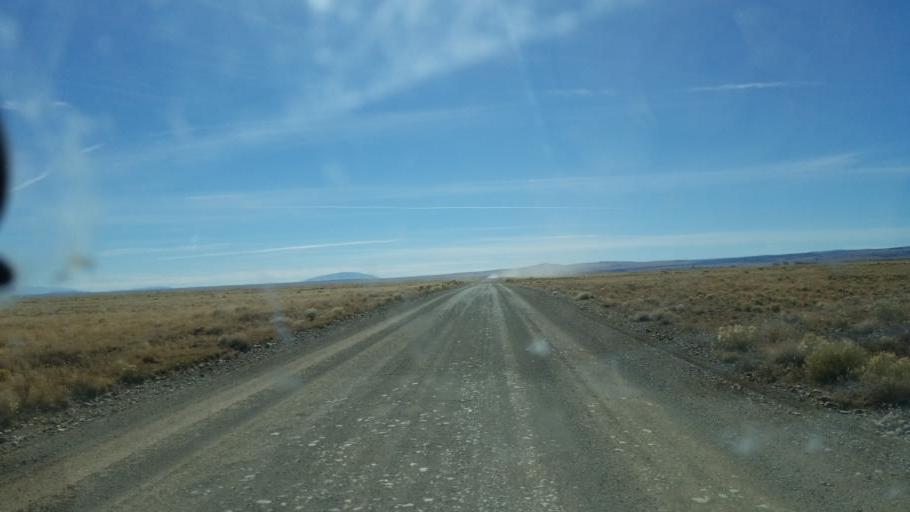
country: US
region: Colorado
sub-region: Rio Grande County
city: Monte Vista
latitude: 37.3373
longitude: -106.1490
